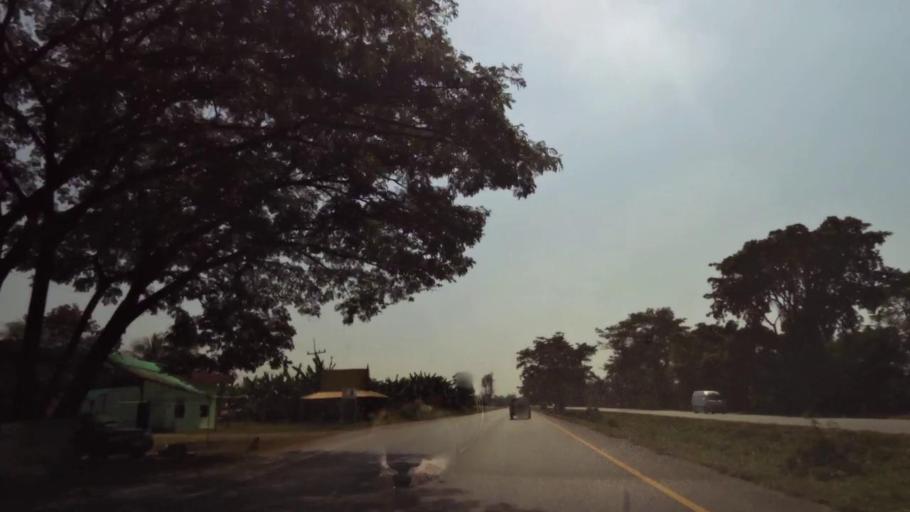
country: TH
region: Phichit
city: Bueng Na Rang
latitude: 16.3369
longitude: 100.1284
